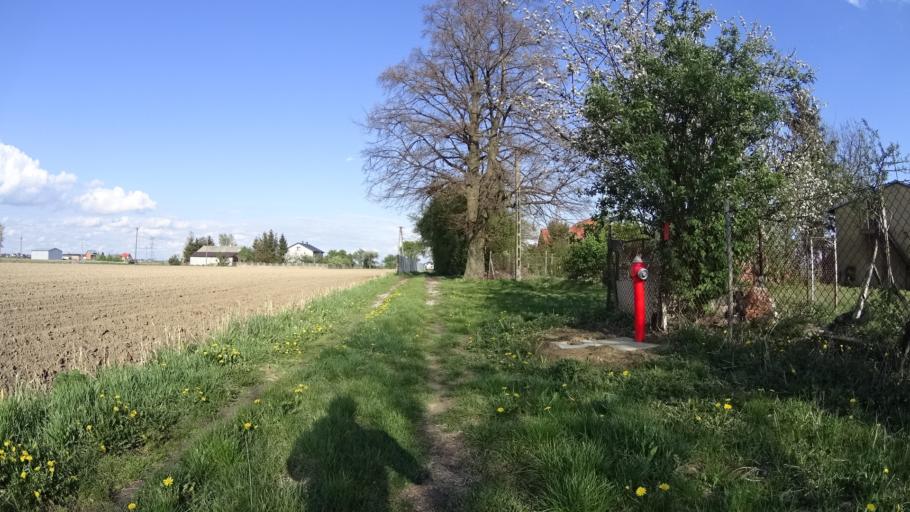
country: PL
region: Masovian Voivodeship
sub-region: Powiat warszawski zachodni
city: Jozefow
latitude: 52.2313
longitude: 20.7310
